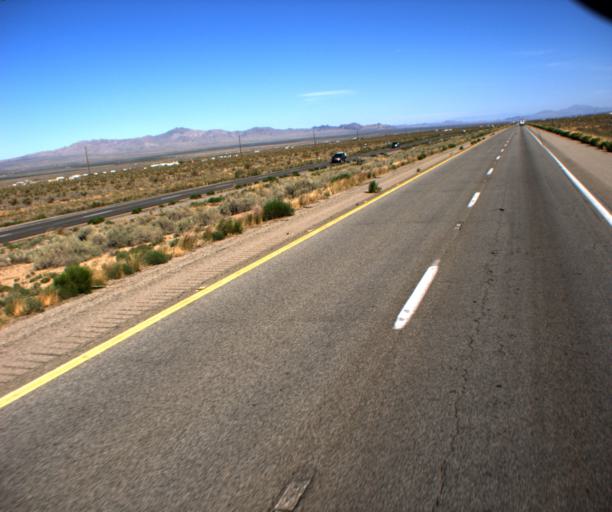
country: US
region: Arizona
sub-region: Mohave County
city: Dolan Springs
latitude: 35.4825
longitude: -114.3196
